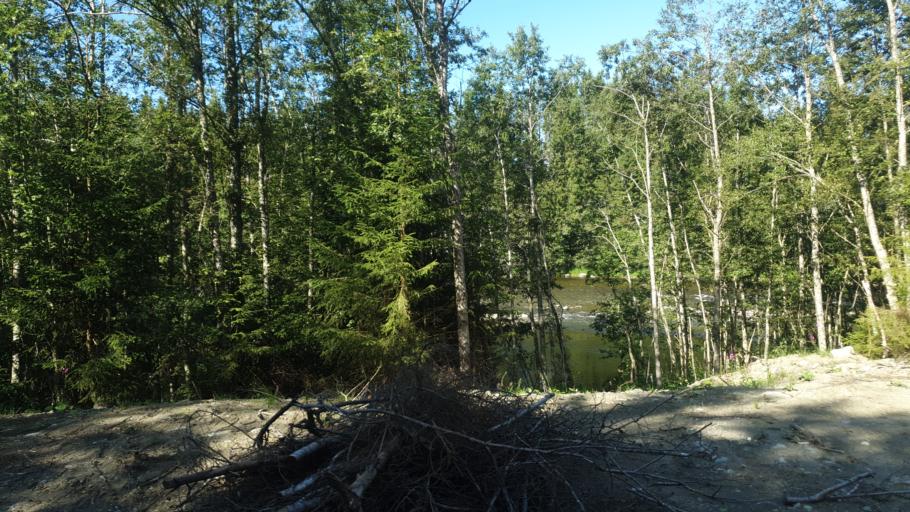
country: NO
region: Sor-Trondelag
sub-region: Orkdal
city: Orkanger
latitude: 63.1860
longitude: 9.7746
